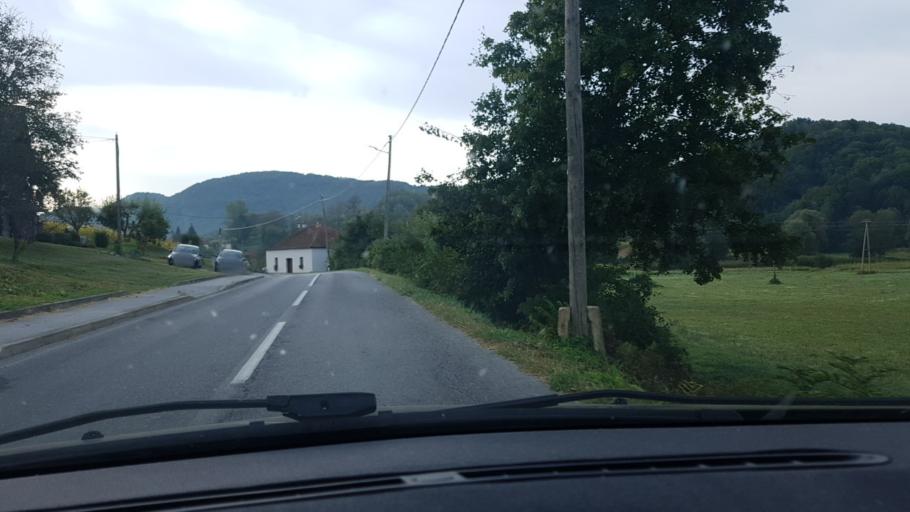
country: HR
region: Krapinsko-Zagorska
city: Mihovljan
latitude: 46.1294
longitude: 15.9711
